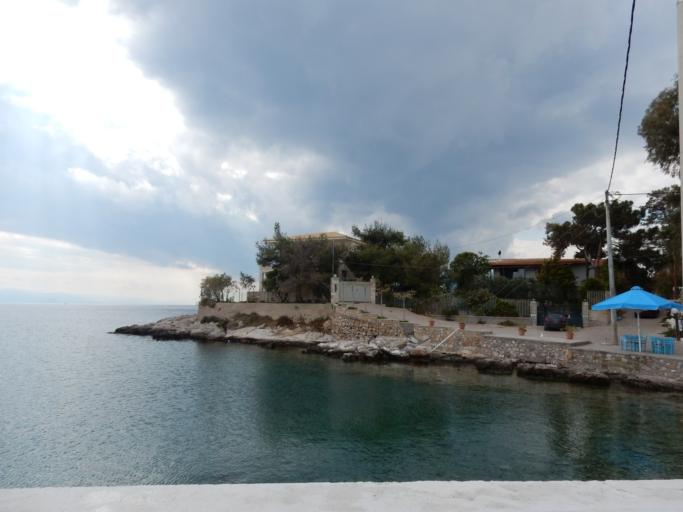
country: GR
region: Attica
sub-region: Nomarchia Dytikis Attikis
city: Megara
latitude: 37.9729
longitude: 23.3614
